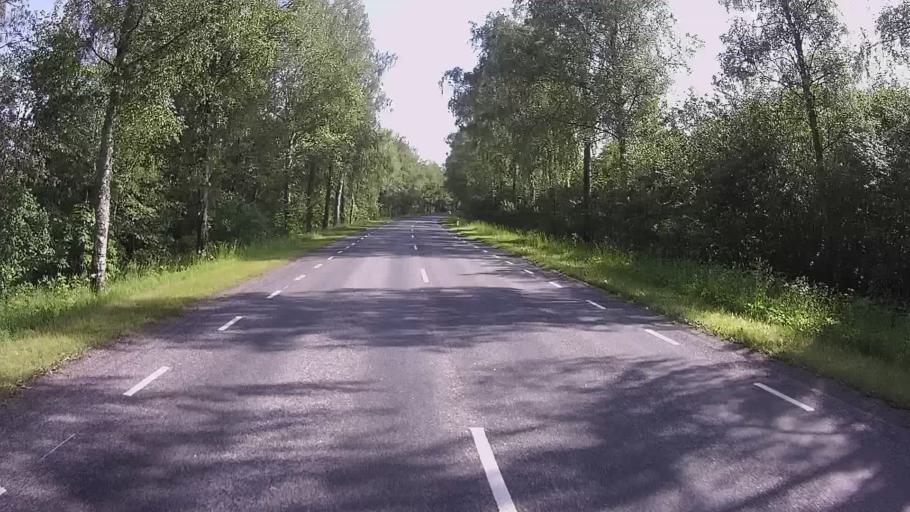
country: EE
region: Valgamaa
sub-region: Torva linn
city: Torva
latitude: 58.0724
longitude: 26.0362
